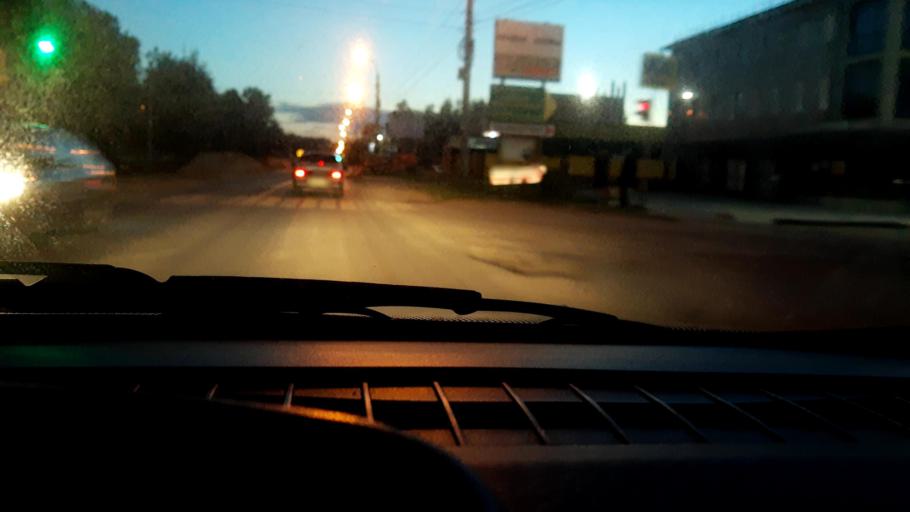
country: RU
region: Nizjnij Novgorod
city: Dzerzhinsk
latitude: 56.2469
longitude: 43.4001
